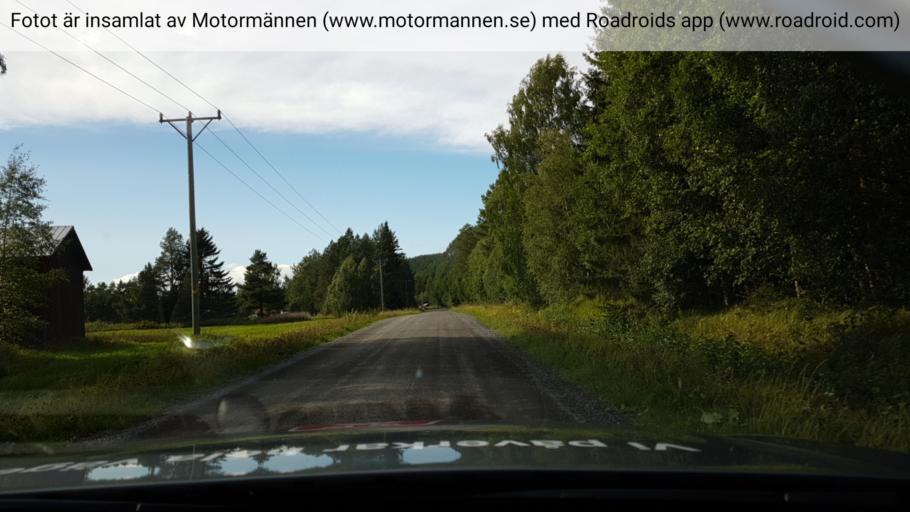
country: SE
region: Jaemtland
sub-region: Braecke Kommun
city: Braecke
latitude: 63.2051
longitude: 15.4081
